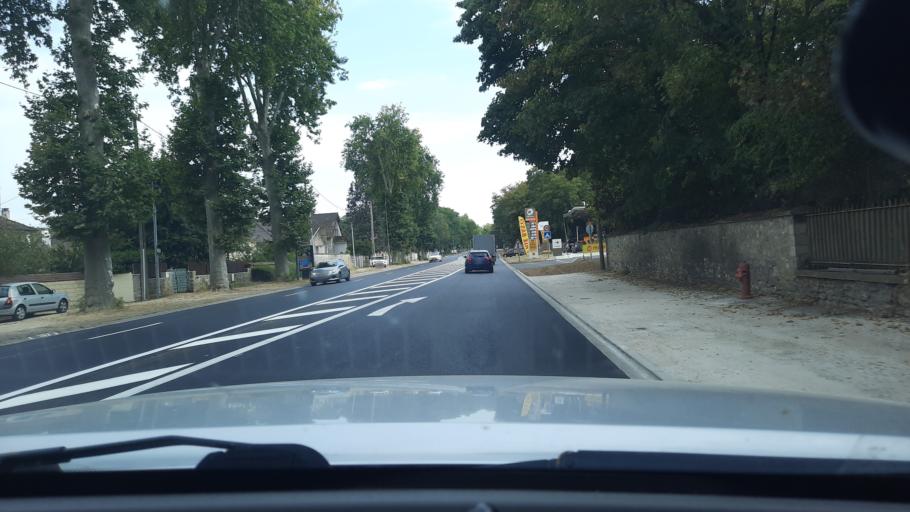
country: FR
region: Ile-de-France
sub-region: Departement de Seine-et-Marne
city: Dammarie-les-Lys
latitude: 48.5197
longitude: 2.6544
